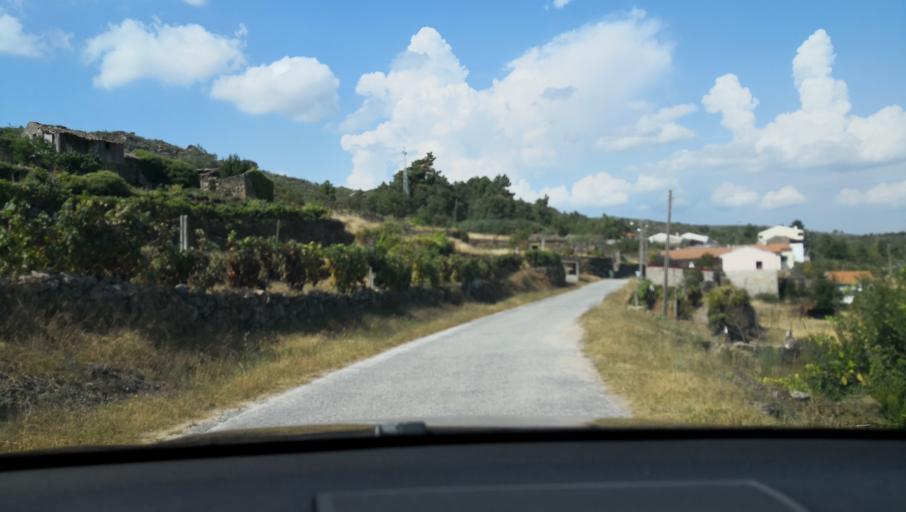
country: PT
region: Vila Real
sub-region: Sabrosa
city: Sabrosa
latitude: 41.3016
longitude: -7.5931
